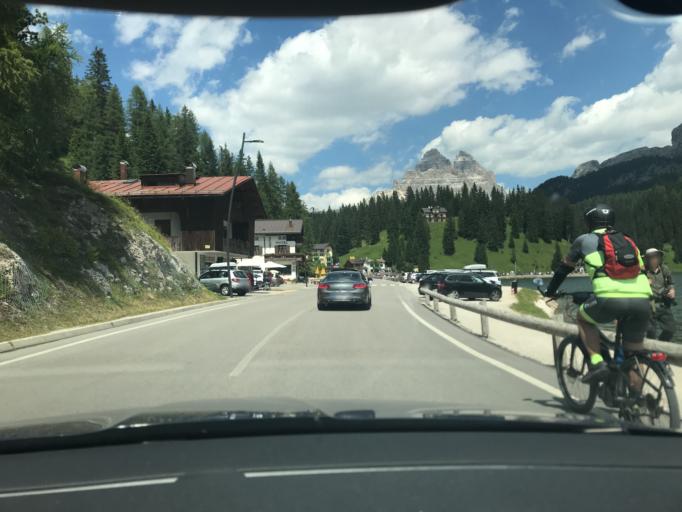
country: IT
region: Veneto
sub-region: Provincia di Belluno
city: Cortina d'Ampezzo
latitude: 46.5820
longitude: 12.2519
